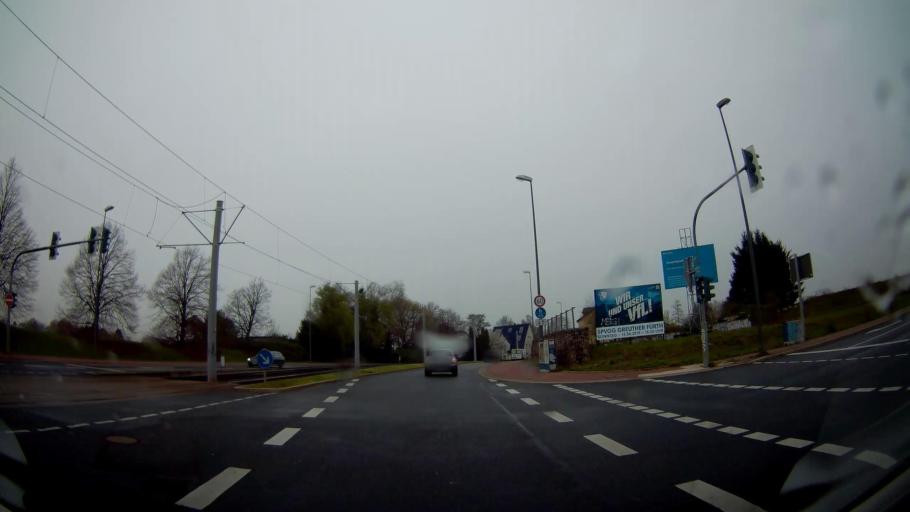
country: DE
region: North Rhine-Westphalia
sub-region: Regierungsbezirk Arnsberg
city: Herne
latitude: 51.5123
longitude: 7.2678
